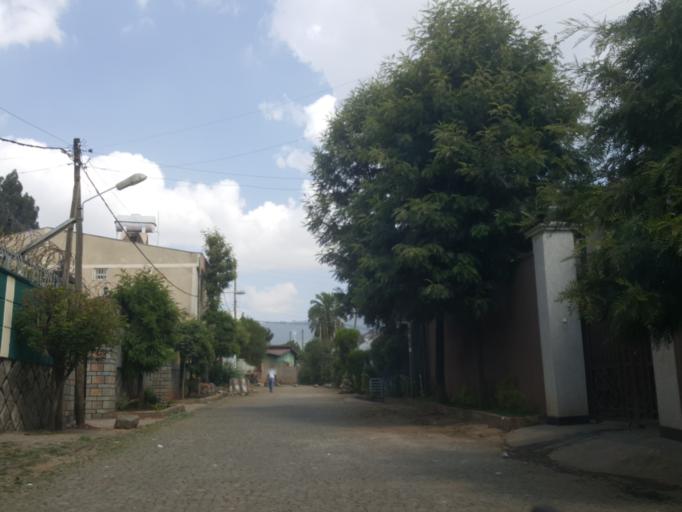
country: ET
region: Adis Abeba
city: Addis Ababa
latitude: 9.0576
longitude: 38.7197
